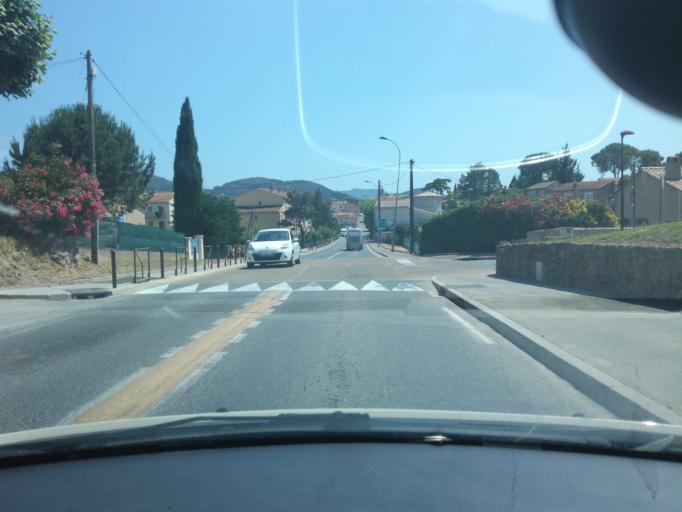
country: FR
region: Provence-Alpes-Cote d'Azur
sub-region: Departement du Var
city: Le Muy
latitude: 43.4775
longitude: 6.5666
